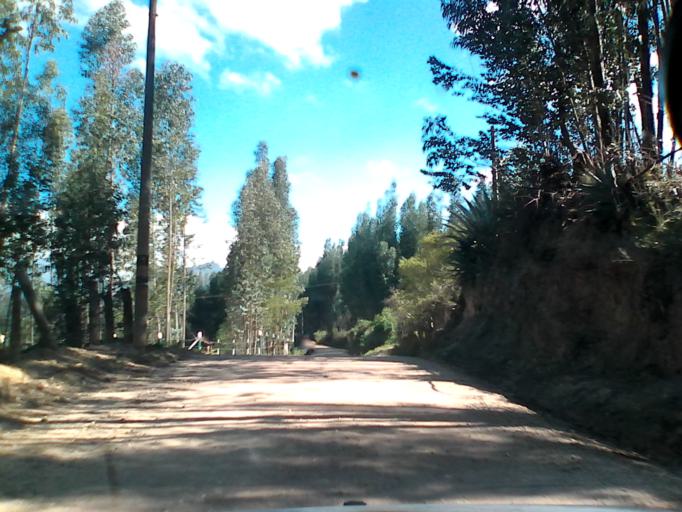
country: CO
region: Boyaca
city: Tibasosa
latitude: 5.7831
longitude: -73.0174
